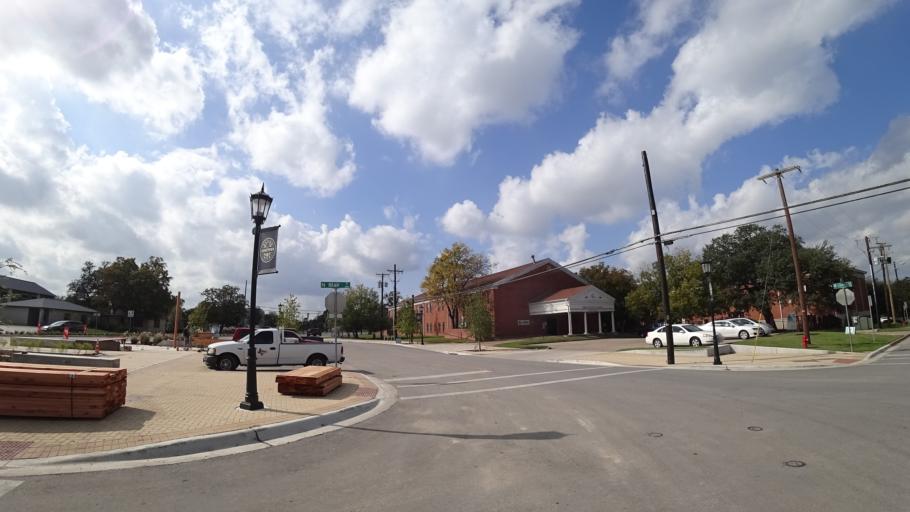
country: US
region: Texas
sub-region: Williamson County
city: Round Rock
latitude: 30.5091
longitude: -97.6802
